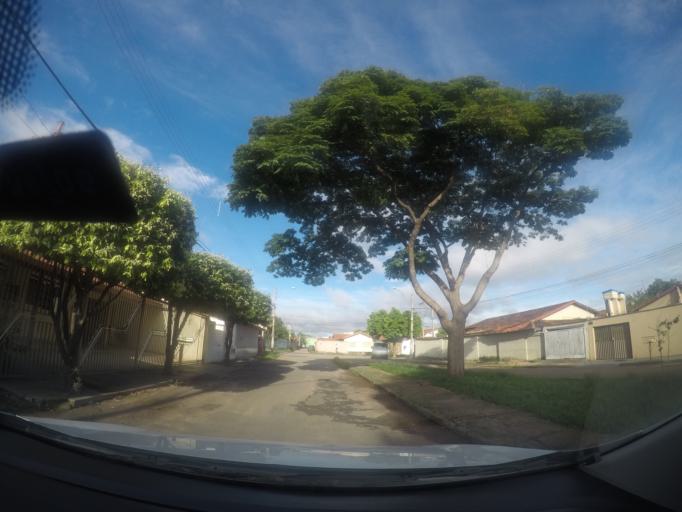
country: BR
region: Goias
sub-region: Goiania
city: Goiania
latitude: -16.6884
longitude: -49.3127
